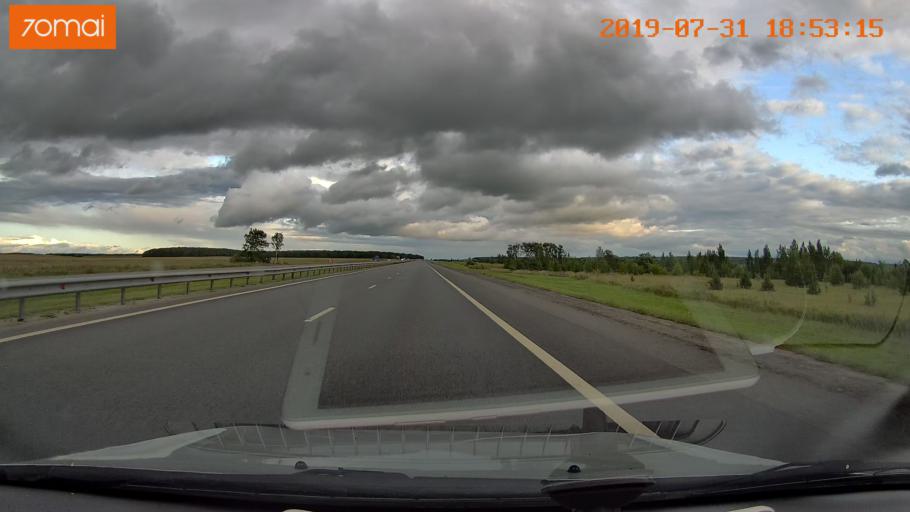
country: RU
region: Moskovskaya
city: Raduzhnyy
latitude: 55.2049
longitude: 38.6492
